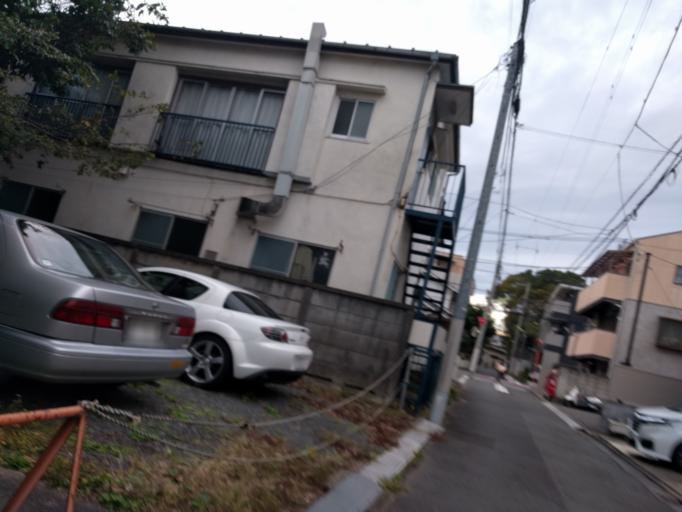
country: JP
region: Tokyo
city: Tokyo
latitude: 35.6407
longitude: 139.6486
